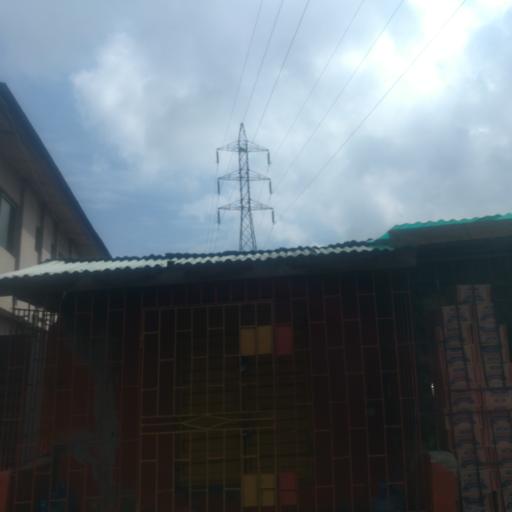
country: NG
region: Lagos
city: Ojota
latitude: 6.6026
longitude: 3.3905
